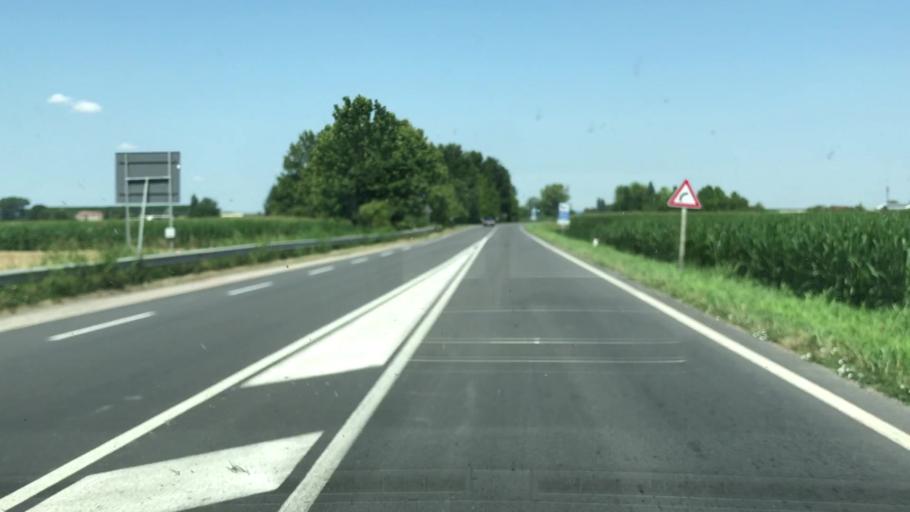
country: IT
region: Veneto
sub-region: Provincia di Rovigo
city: Castelnovo Bariano
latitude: 45.0345
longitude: 11.2975
